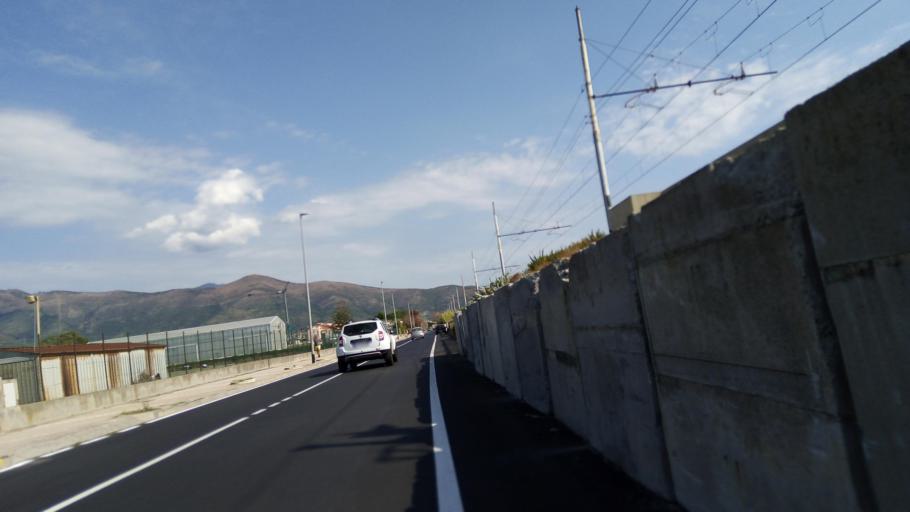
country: IT
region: Liguria
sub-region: Provincia di Savona
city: Albenga
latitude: 44.0659
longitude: 8.2249
